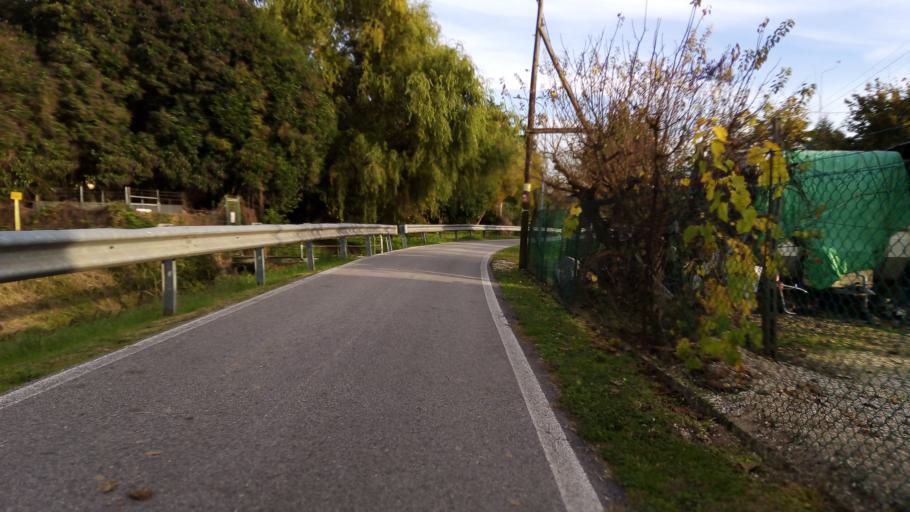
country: IT
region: Veneto
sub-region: Provincia di Padova
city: Mandriola-Sant'Agostino
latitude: 45.3628
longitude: 11.8204
